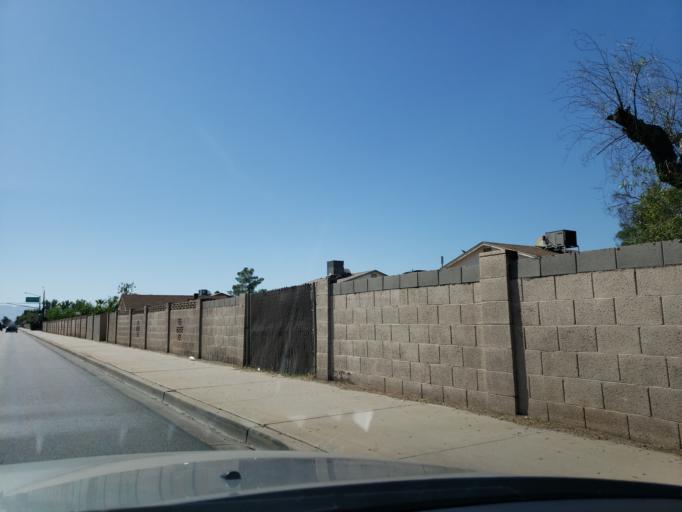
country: US
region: Arizona
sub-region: Maricopa County
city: Tolleson
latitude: 33.4852
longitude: -112.2207
